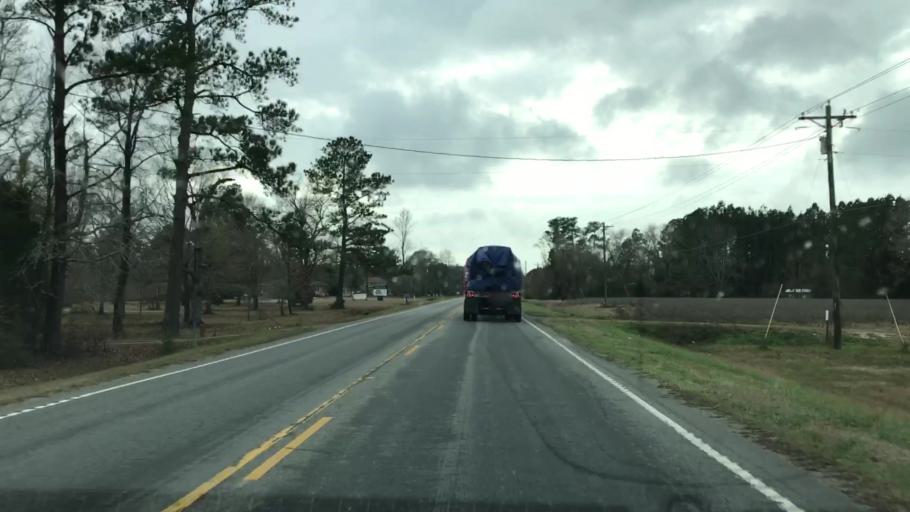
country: US
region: South Carolina
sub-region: Berkeley County
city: Saint Stephen
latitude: 33.2852
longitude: -79.8662
